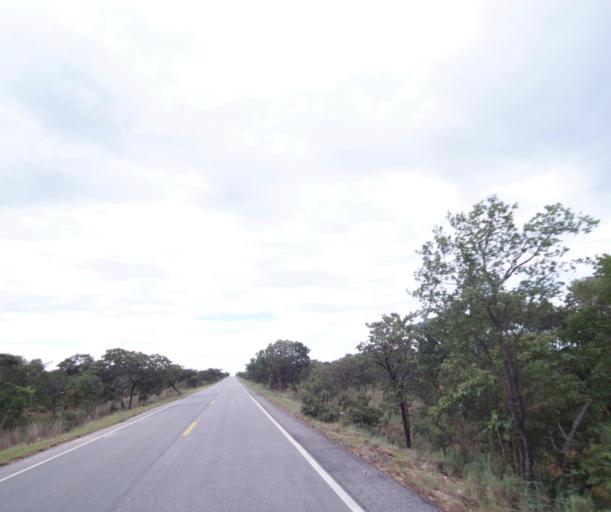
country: BR
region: Bahia
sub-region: Sao Felix Do Coribe
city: Santa Maria da Vitoria
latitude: -13.9618
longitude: -44.4459
